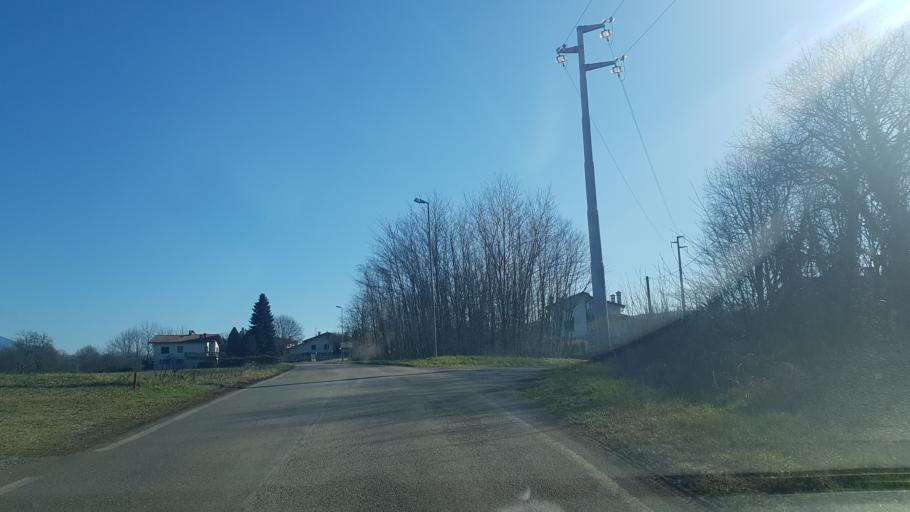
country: IT
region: Friuli Venezia Giulia
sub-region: Provincia di Gorizia
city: Savogna d'Isonzo
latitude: 45.8971
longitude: 13.5757
